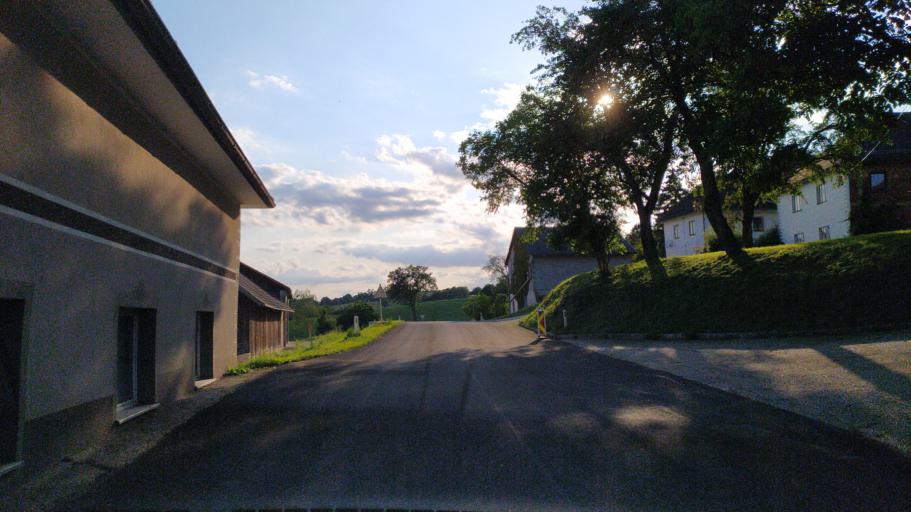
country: AT
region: Lower Austria
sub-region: Politischer Bezirk Amstetten
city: Strengberg
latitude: 48.1505
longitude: 14.6701
